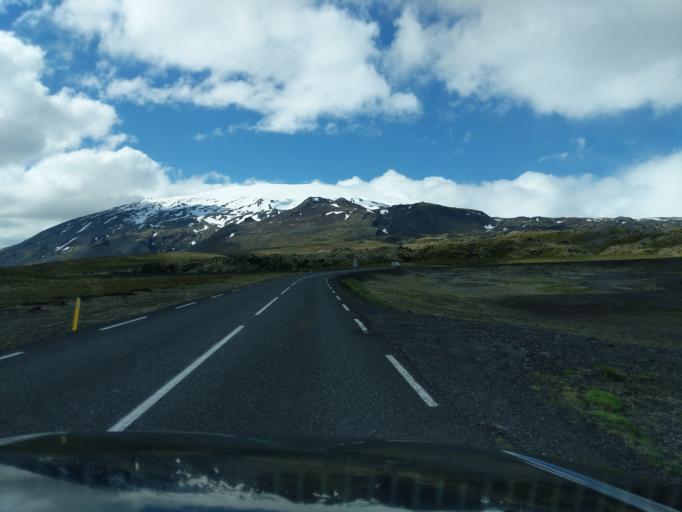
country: IS
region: West
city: Olafsvik
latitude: 64.7610
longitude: -23.6752
